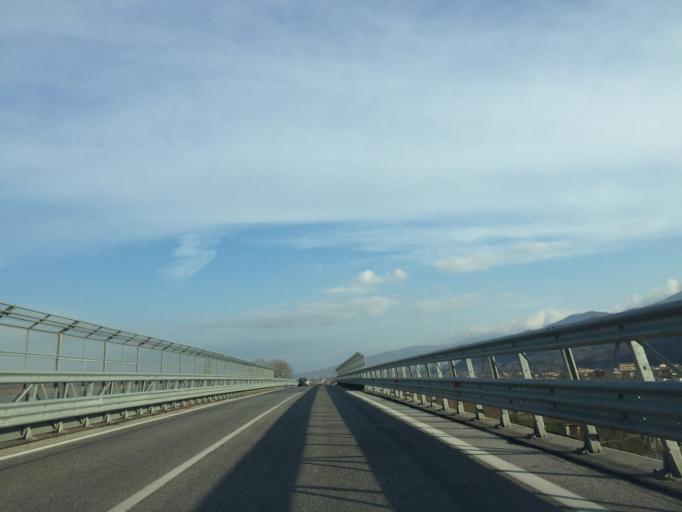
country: IT
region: Molise
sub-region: Provincia di Campobasso
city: Bojano
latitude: 41.4968
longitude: 14.4646
